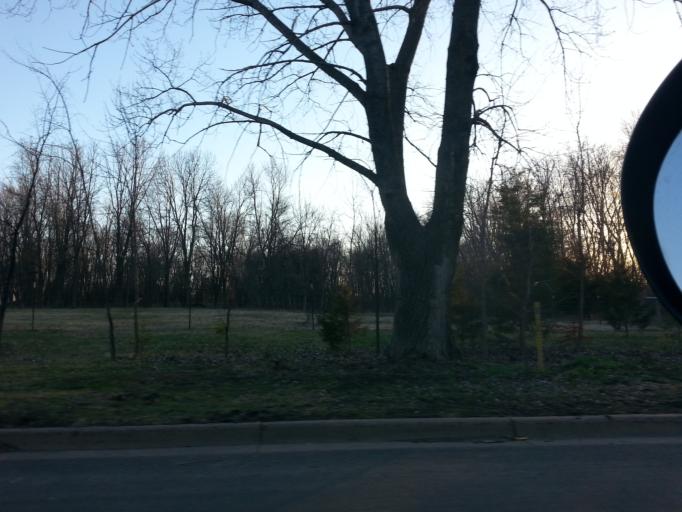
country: US
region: Minnesota
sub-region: Scott County
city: Prior Lake
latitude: 44.7005
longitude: -93.4317
